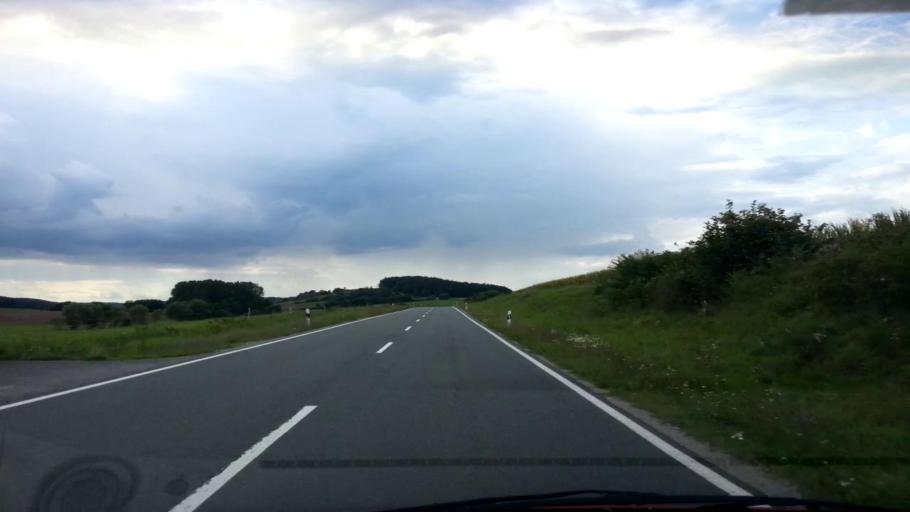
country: DE
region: Bavaria
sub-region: Regierungsbezirk Mittelfranken
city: Burghaslach
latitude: 49.7334
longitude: 10.5864
